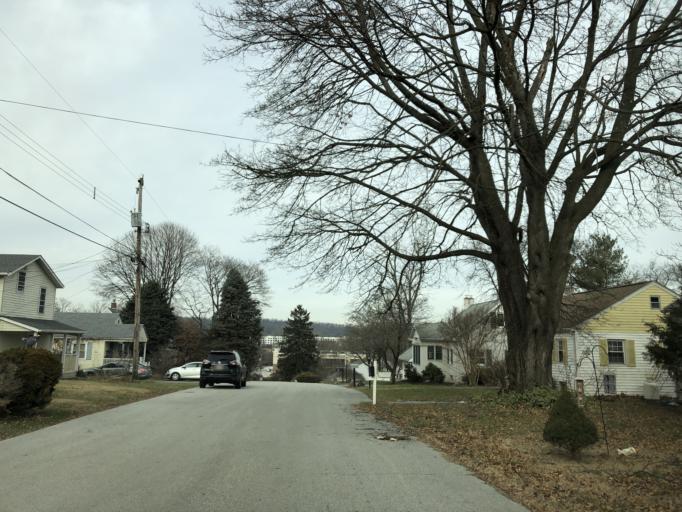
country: US
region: Pennsylvania
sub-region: Chester County
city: Exton
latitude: 40.0245
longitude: -75.6243
